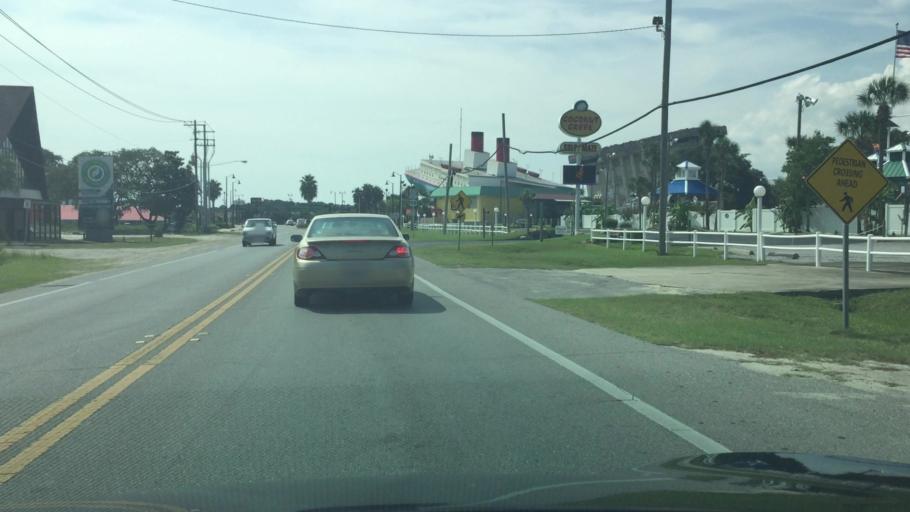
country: US
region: Florida
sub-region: Bay County
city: Panama City Beach
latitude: 30.1771
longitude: -85.7976
